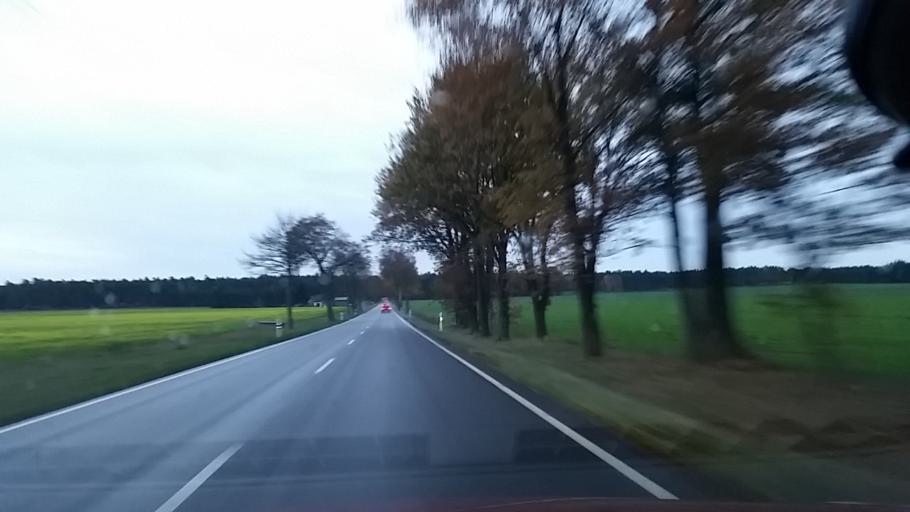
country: DE
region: Lower Saxony
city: Bodenteich
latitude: 52.7922
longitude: 10.7153
